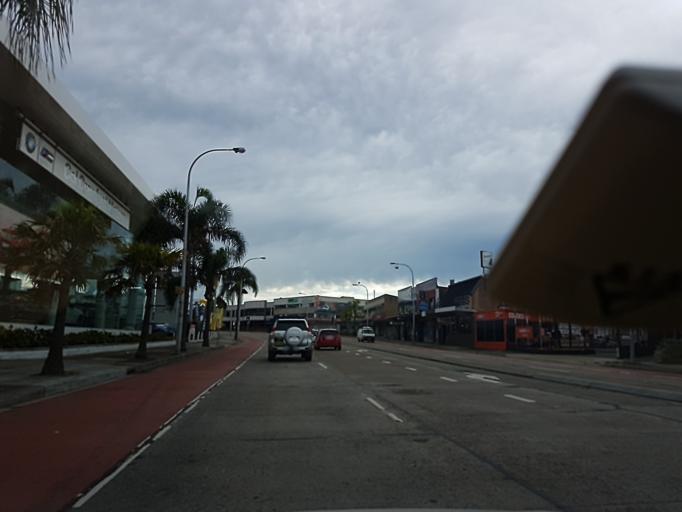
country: AU
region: New South Wales
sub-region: Warringah
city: Brookvale
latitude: -33.7650
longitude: 151.2705
